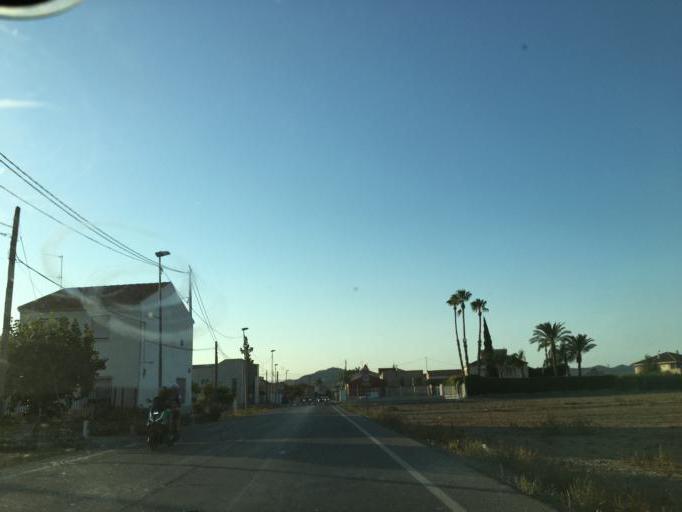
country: ES
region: Murcia
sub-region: Murcia
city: Murcia
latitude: 38.0045
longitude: -1.0781
